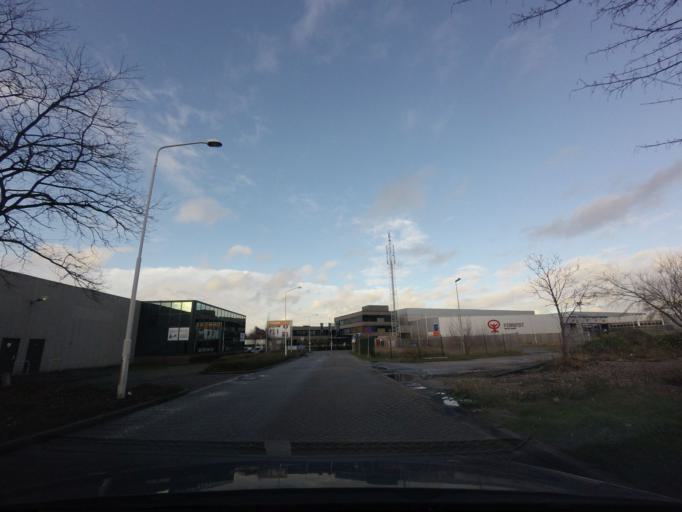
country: NL
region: South Holland
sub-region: Gemeente Rotterdam
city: Rotterdam
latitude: 51.9418
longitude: 4.4971
